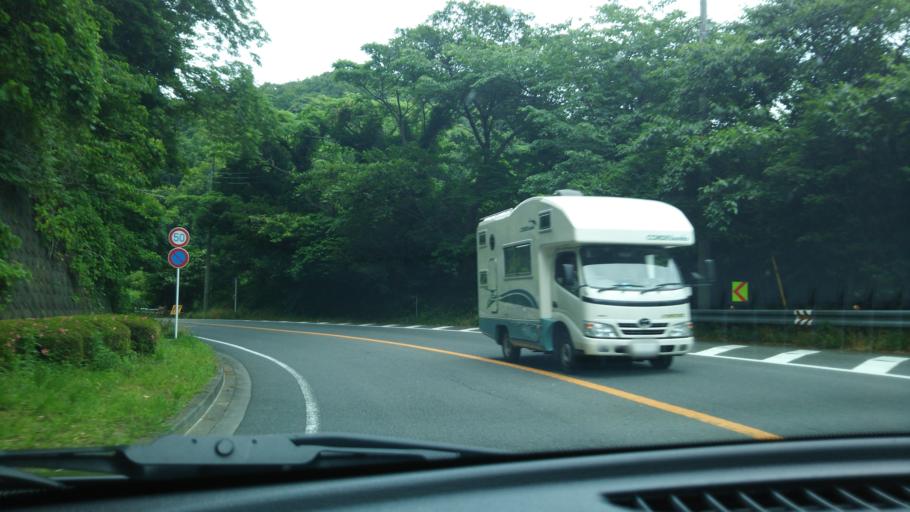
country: JP
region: Shizuoka
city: Ito
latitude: 34.8228
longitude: 139.0757
